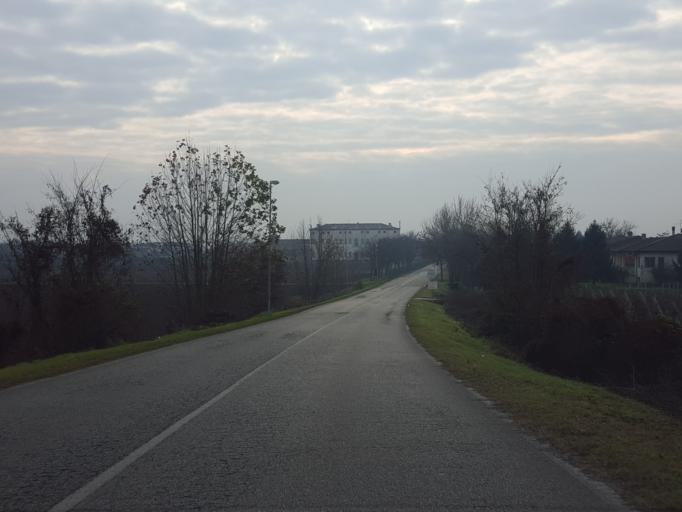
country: IT
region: Veneto
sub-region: Provincia di Verona
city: San Bonifacio
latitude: 45.4054
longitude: 11.3080
